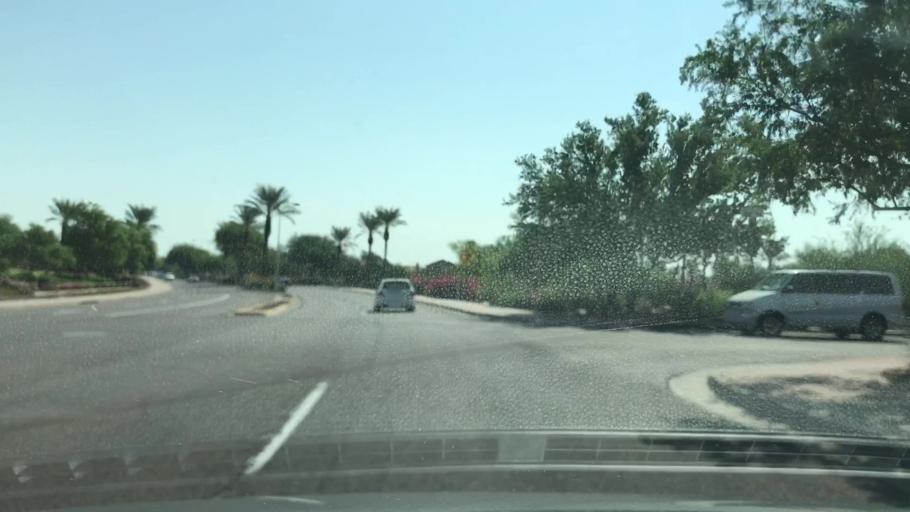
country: US
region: Arizona
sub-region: Maricopa County
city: Guadalupe
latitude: 33.3042
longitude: -112.0229
